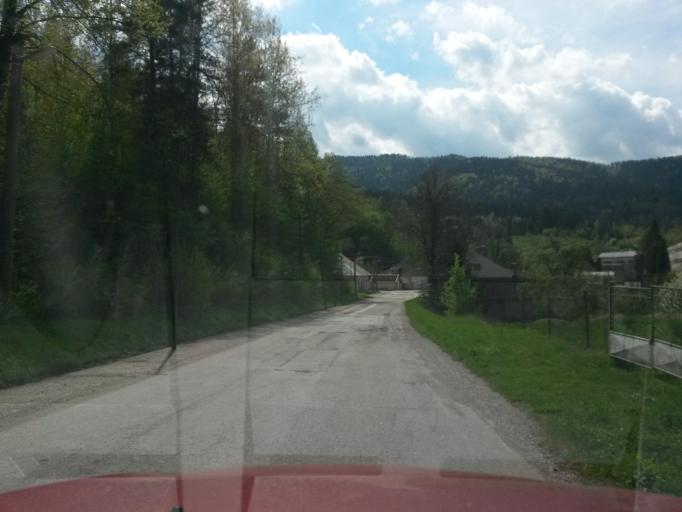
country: SK
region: Kosicky
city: Gelnica
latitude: 48.8158
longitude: 20.8986
